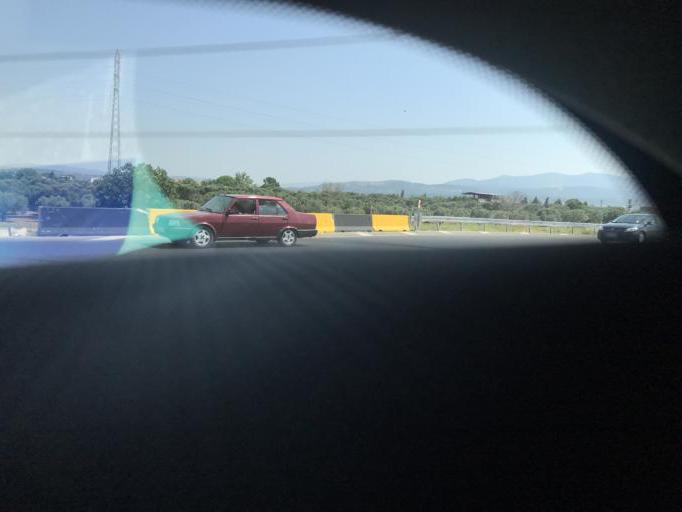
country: TR
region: Manisa
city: Akhisar
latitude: 38.9540
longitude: 27.8207
